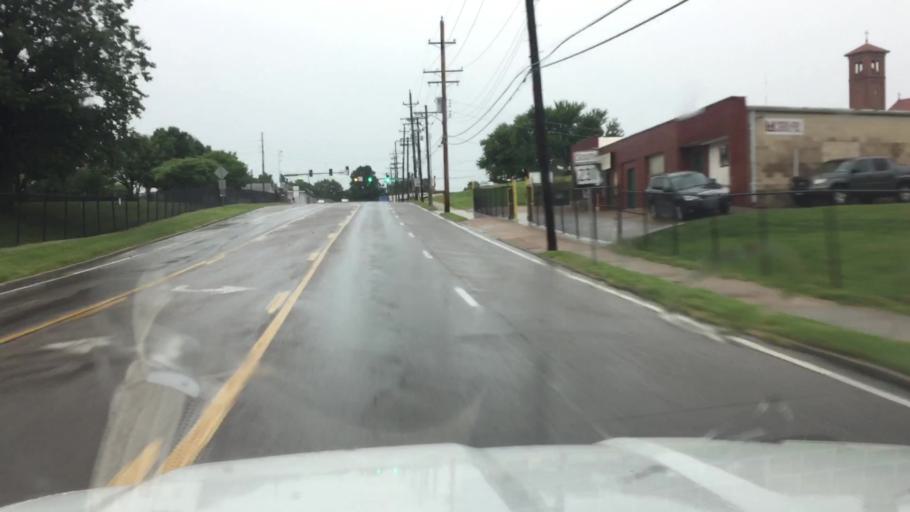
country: US
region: Missouri
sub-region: Saint Louis County
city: Lemay
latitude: 38.5344
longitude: -90.2737
